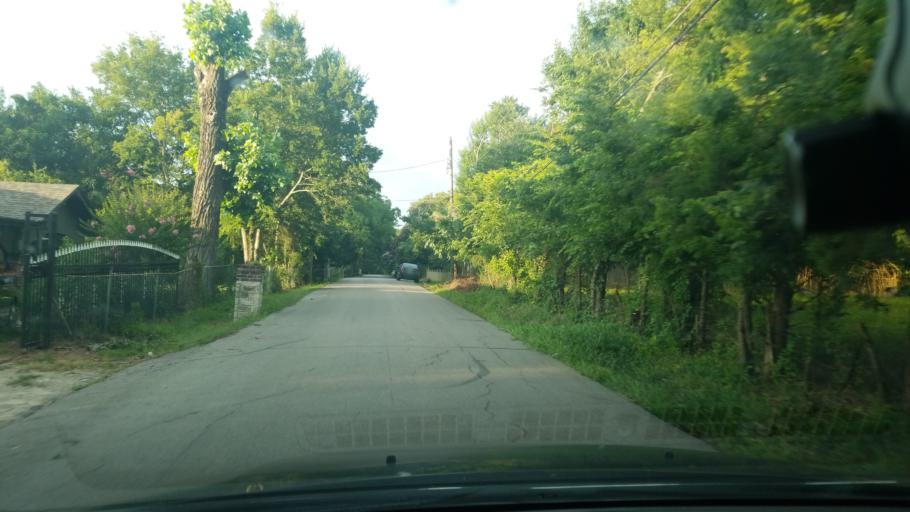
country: US
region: Texas
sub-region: Dallas County
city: Balch Springs
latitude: 32.7481
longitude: -96.6376
